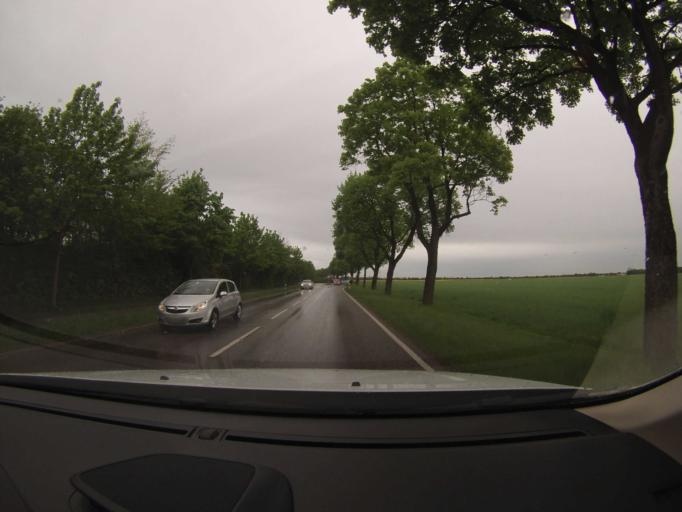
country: DE
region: Bavaria
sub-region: Upper Bavaria
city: Taufkirchen
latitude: 48.0434
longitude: 11.6299
